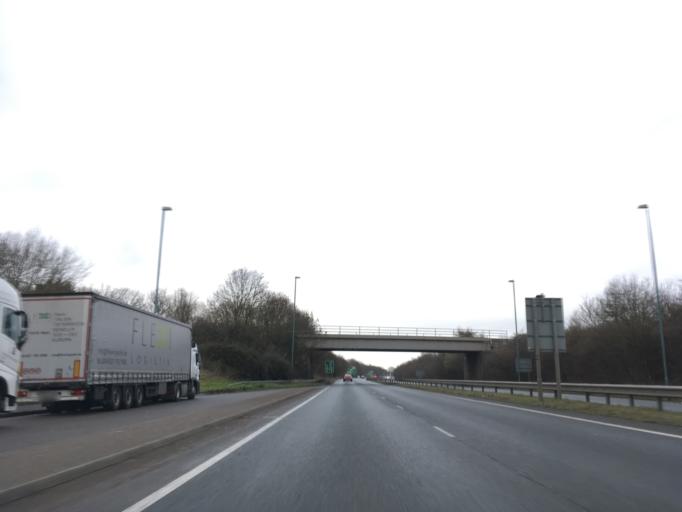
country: GB
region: England
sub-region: Gloucestershire
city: Barnwood
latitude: 51.8705
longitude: -2.1975
